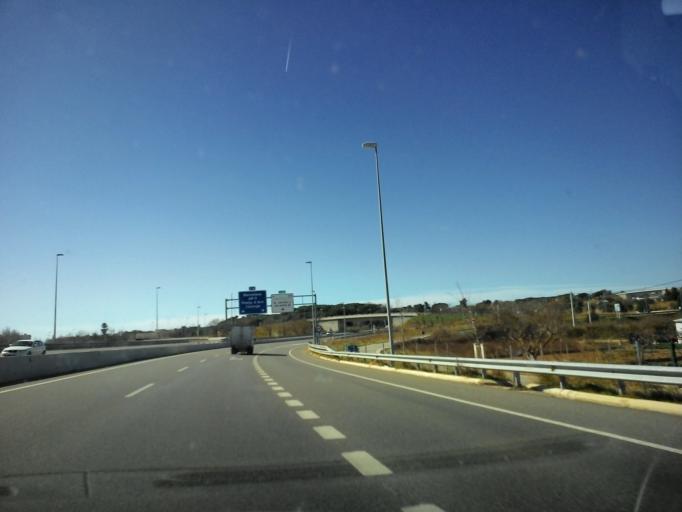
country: ES
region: Catalonia
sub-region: Provincia de Girona
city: Palamos
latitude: 41.8593
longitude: 3.1239
